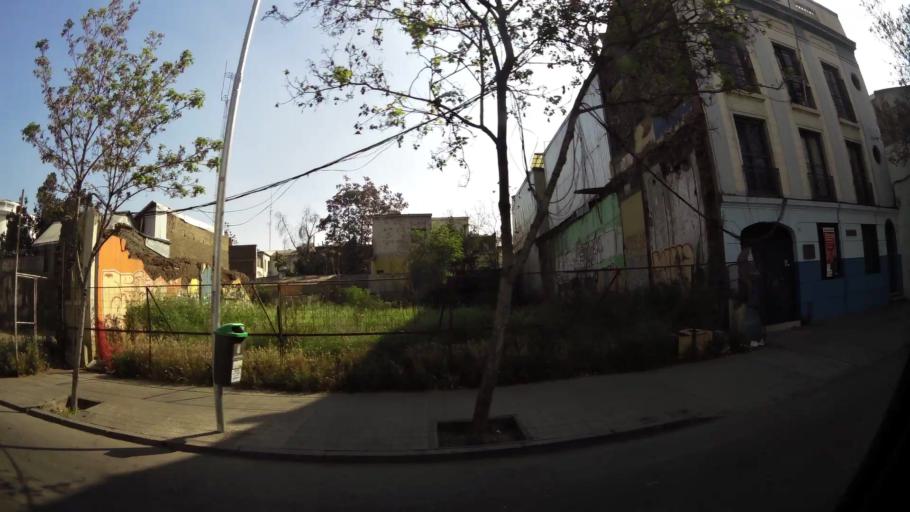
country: CL
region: Santiago Metropolitan
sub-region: Provincia de Santiago
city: Santiago
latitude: -33.4448
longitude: -70.6588
